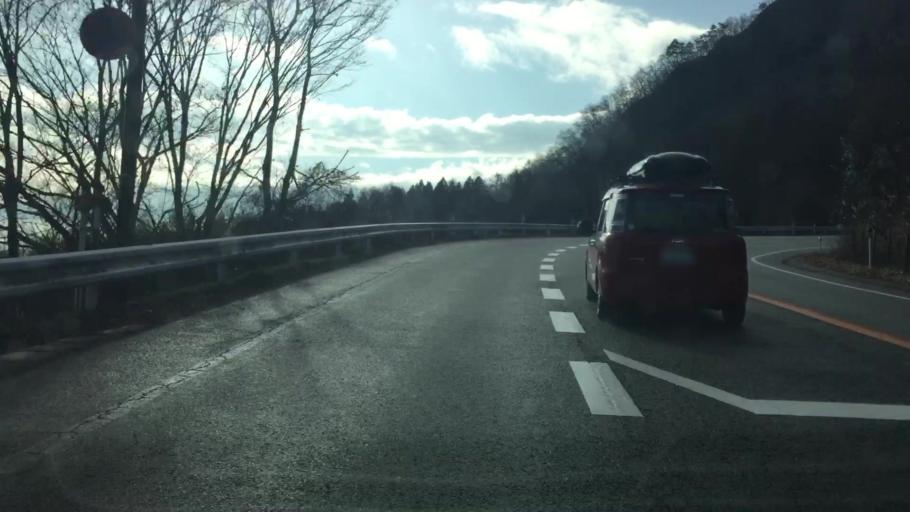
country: JP
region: Nagano
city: Saku
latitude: 36.3023
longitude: 138.6649
